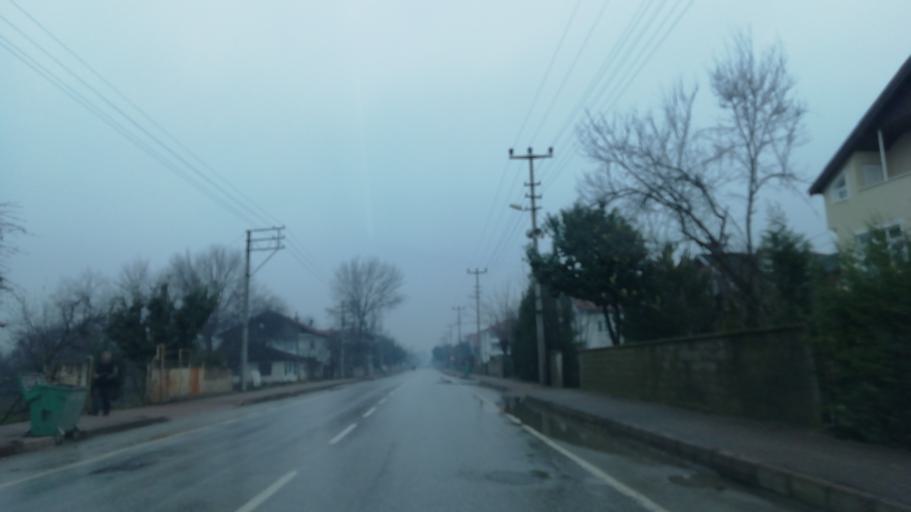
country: TR
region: Sakarya
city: Akyazi
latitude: 40.6624
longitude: 30.6192
